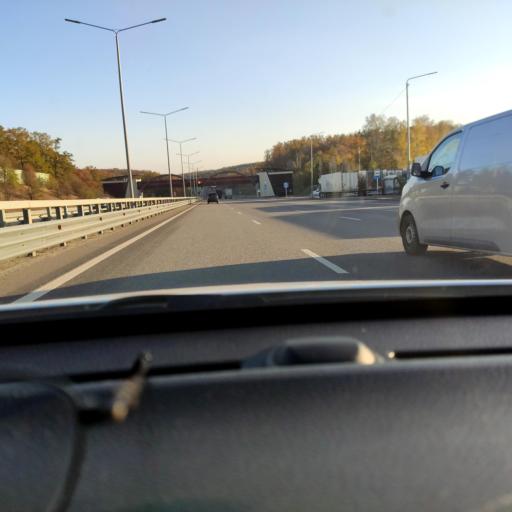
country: RU
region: Voronezj
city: Podgornoye
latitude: 51.8100
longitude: 39.2525
